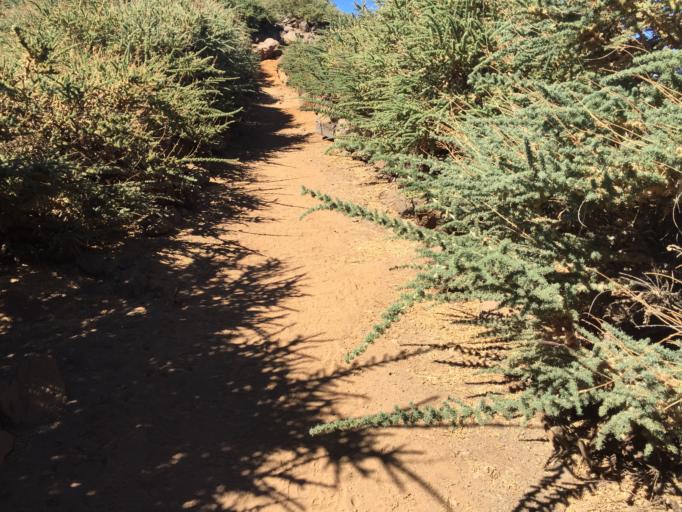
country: ES
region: Canary Islands
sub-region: Provincia de Santa Cruz de Tenerife
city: Barlovento
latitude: 28.7603
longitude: -17.8633
